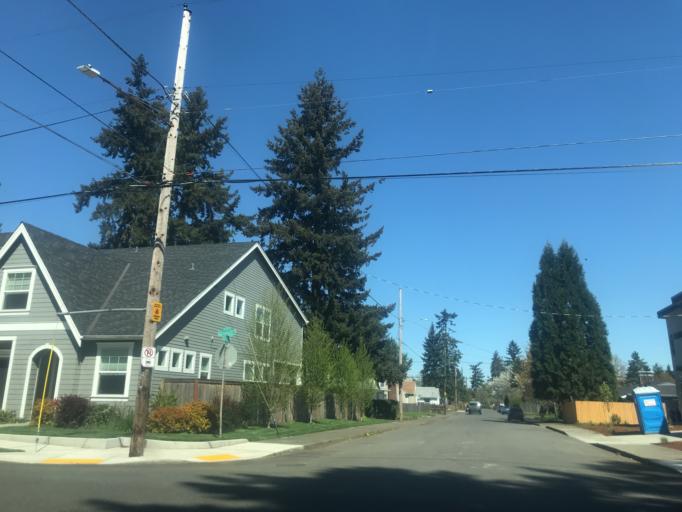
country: US
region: Oregon
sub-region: Multnomah County
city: Lents
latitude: 45.4830
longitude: -122.6047
